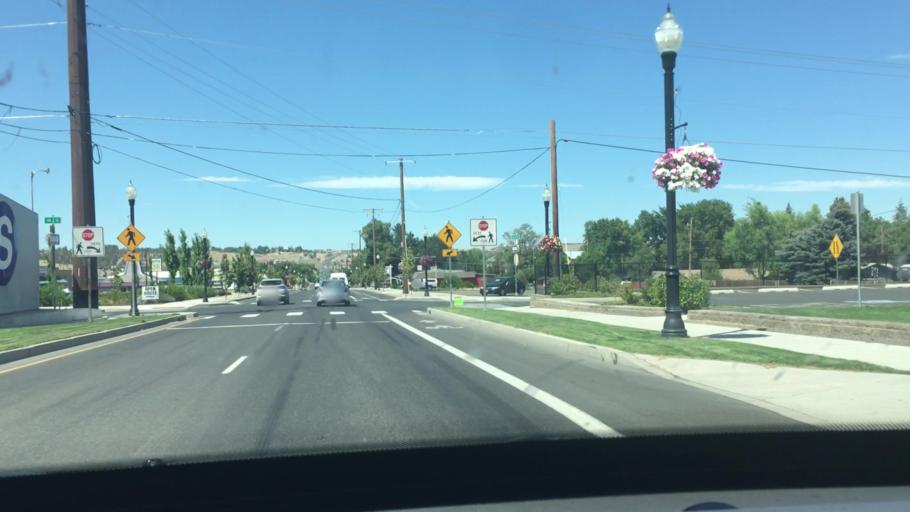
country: US
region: Oregon
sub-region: Jefferson County
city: Madras
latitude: 44.6247
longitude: -121.1296
